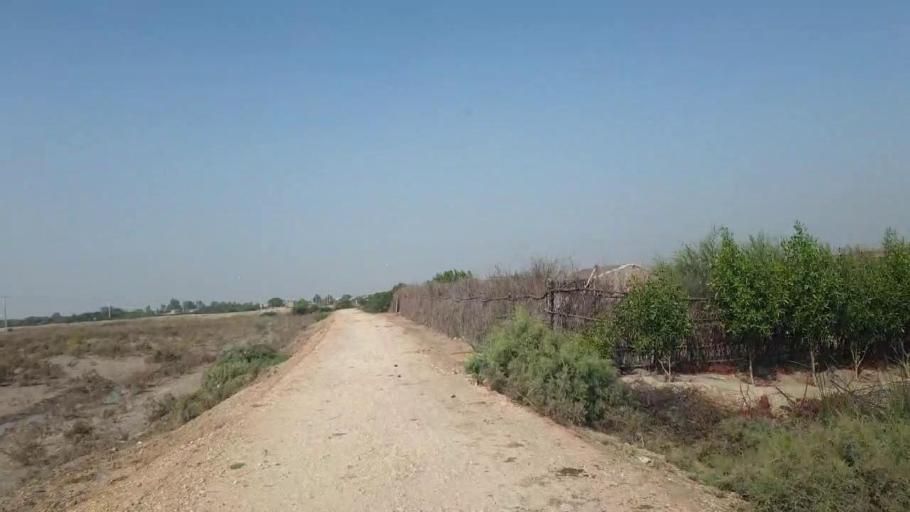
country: PK
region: Sindh
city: Badin
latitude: 24.5211
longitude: 68.7680
